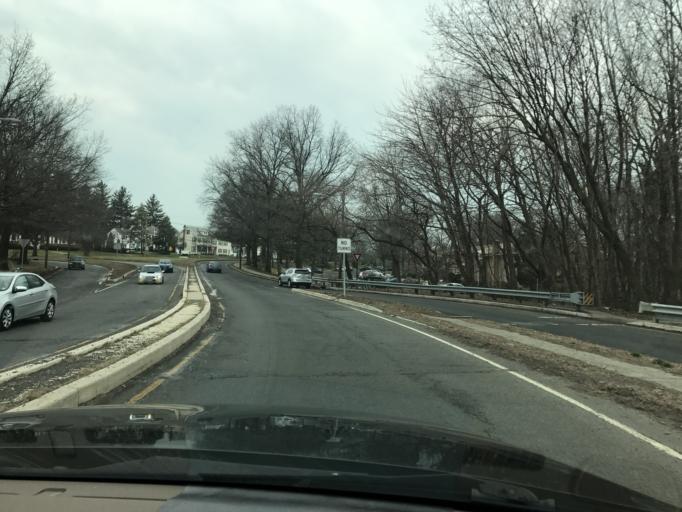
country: US
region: New Jersey
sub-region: Middlesex County
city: South River
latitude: 40.4391
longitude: -74.3943
